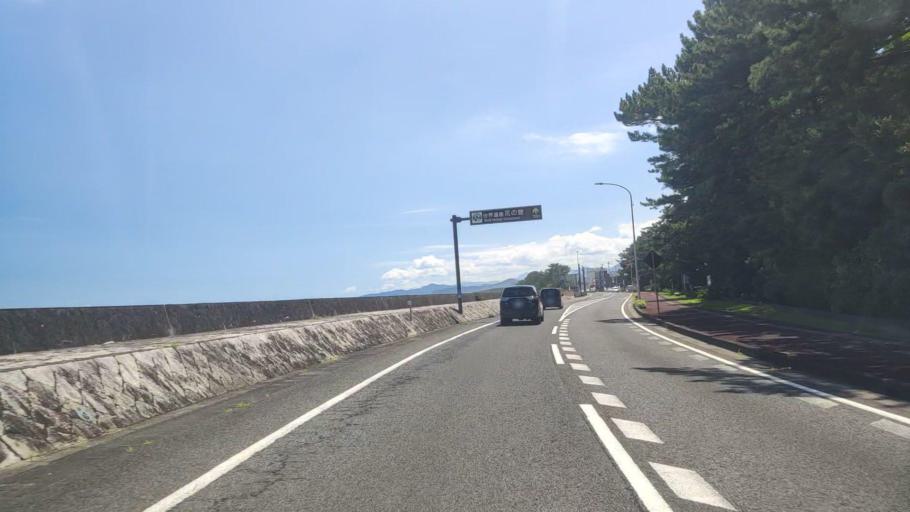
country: JP
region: Wakayama
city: Shingu
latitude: 33.8795
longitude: 136.0938
